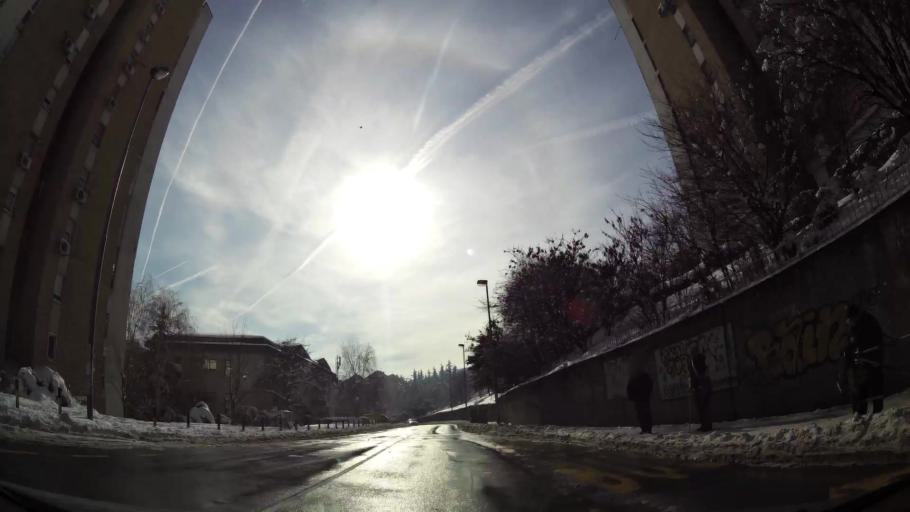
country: RS
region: Central Serbia
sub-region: Belgrade
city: Zvezdara
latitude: 44.7903
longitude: 20.5276
